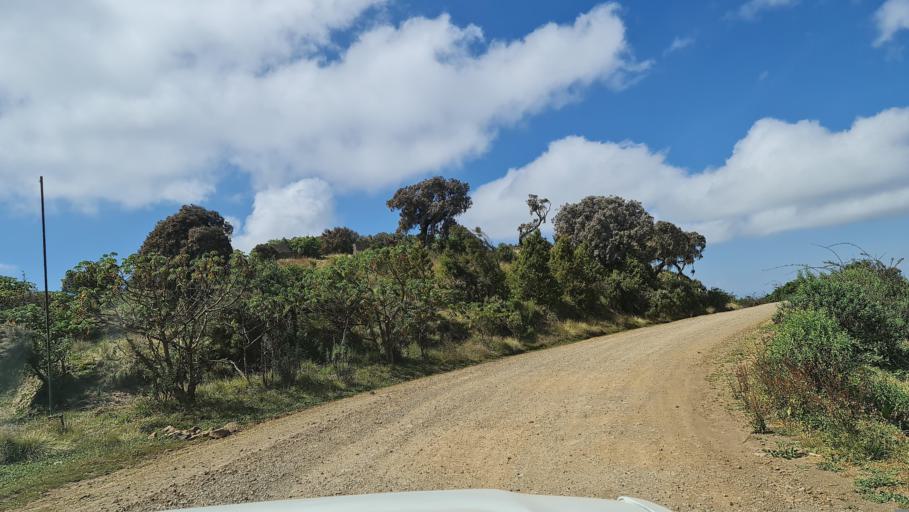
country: ET
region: Amhara
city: Debark'
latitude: 13.2120
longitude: 37.9782
